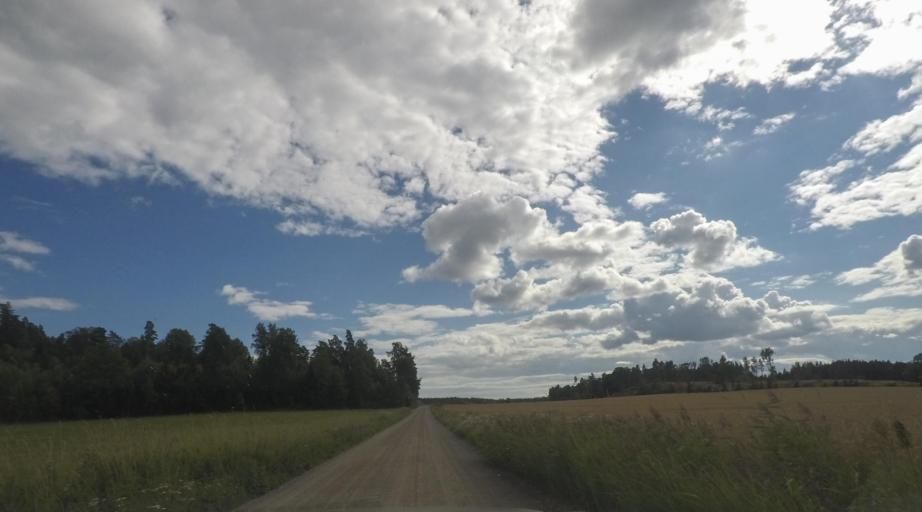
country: SE
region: Stockholm
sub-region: Sodertalje Kommun
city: Pershagen
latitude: 59.1185
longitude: 17.6569
